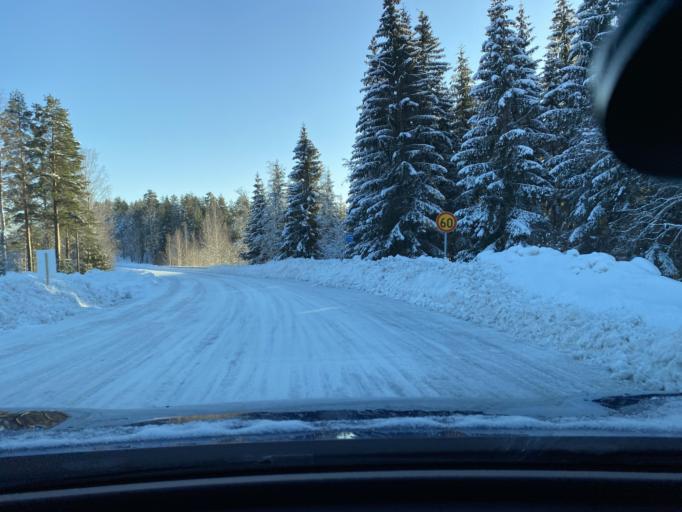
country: FI
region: Southern Savonia
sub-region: Mikkeli
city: Kangasniemi
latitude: 62.0150
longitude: 26.6169
